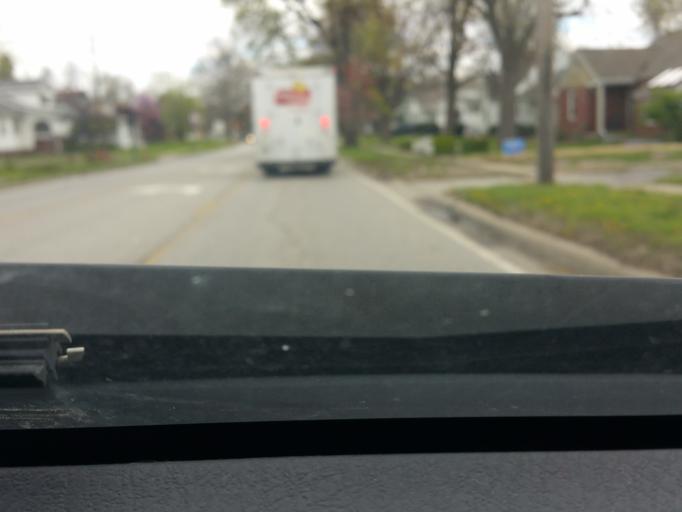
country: US
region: Illinois
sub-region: Madison County
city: Edwardsville
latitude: 38.7967
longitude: -89.9511
